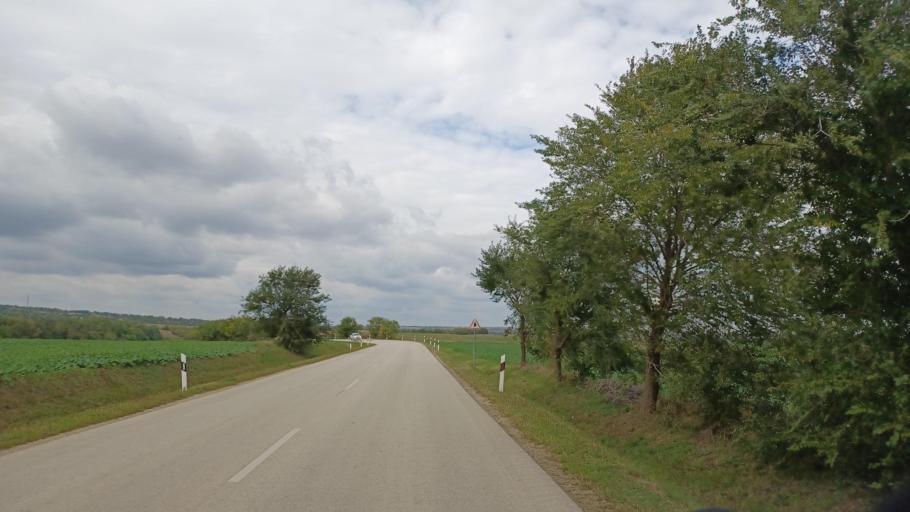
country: HU
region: Tolna
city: Simontornya
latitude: 46.7242
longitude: 18.5754
